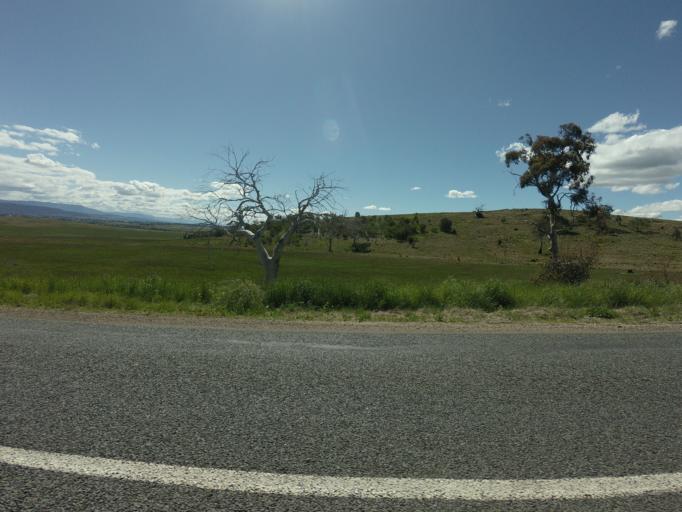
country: AU
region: Tasmania
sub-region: Northern Midlands
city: Evandale
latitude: -41.9373
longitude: 147.5718
